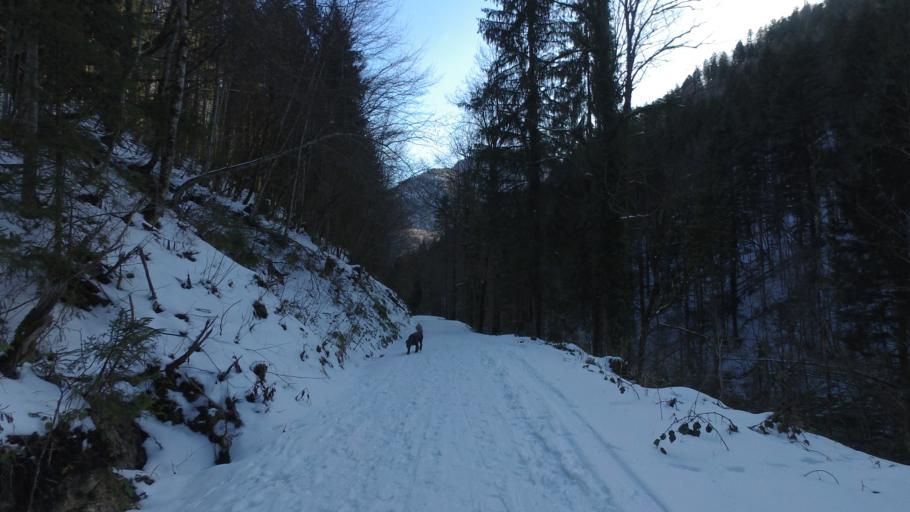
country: DE
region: Bavaria
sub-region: Upper Bavaria
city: Ruhpolding
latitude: 47.7485
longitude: 12.6058
